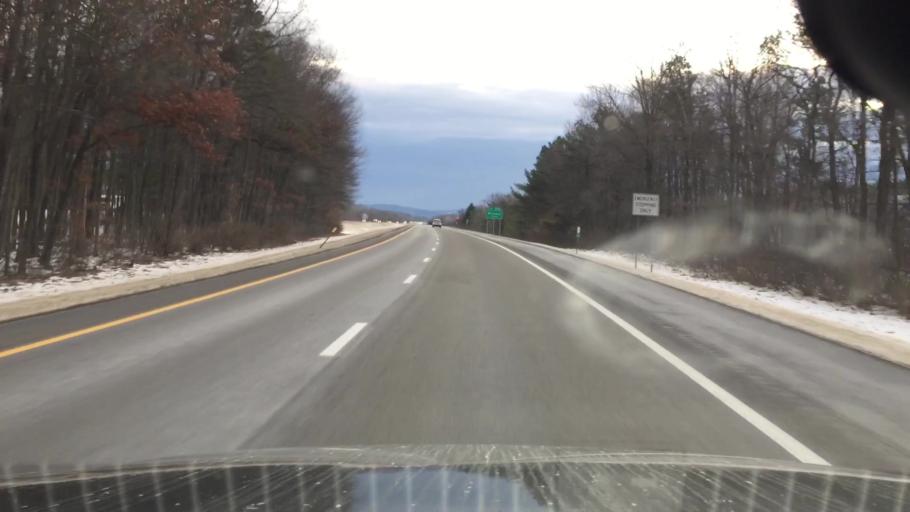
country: US
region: Pennsylvania
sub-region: Bradford County
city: South Waverly
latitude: 42.0008
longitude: -76.6159
